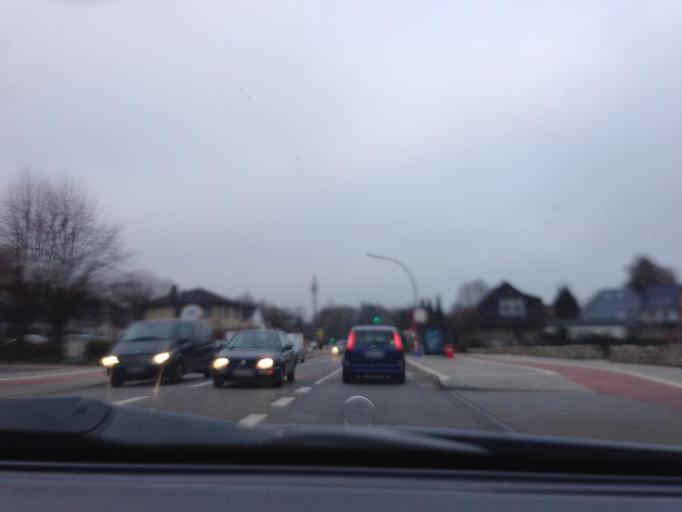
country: DE
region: Hamburg
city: Farmsen-Berne
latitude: 53.6230
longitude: 10.1665
